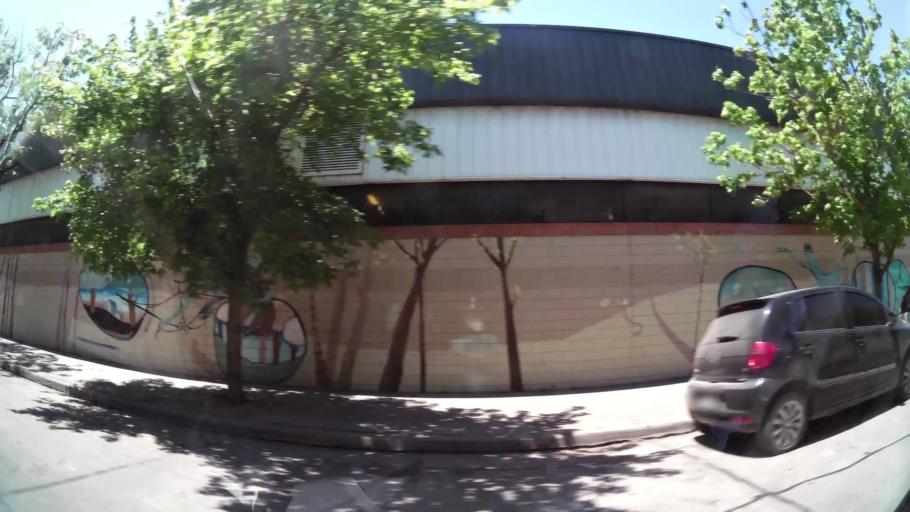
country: AR
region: Buenos Aires
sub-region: Partido de Avellaneda
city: Avellaneda
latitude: -34.6560
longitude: -58.3801
